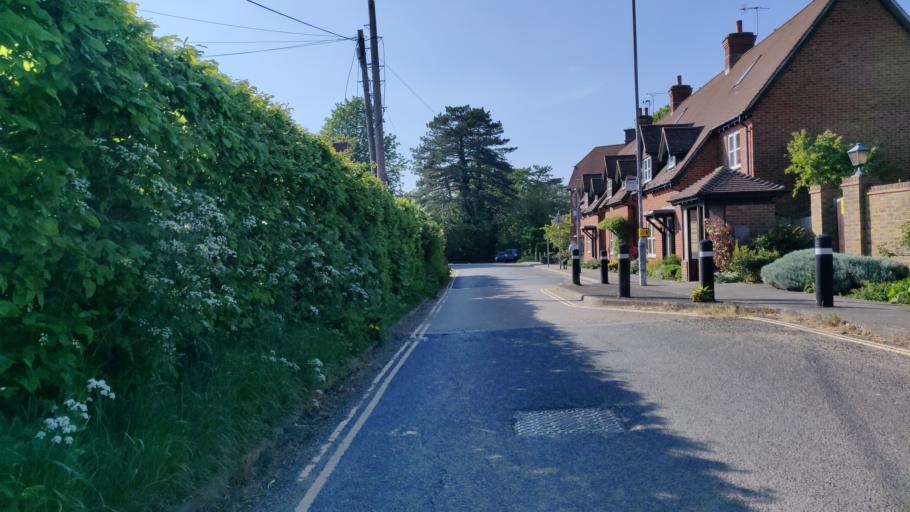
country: GB
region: England
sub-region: West Sussex
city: Southwater
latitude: 51.0479
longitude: -0.3625
